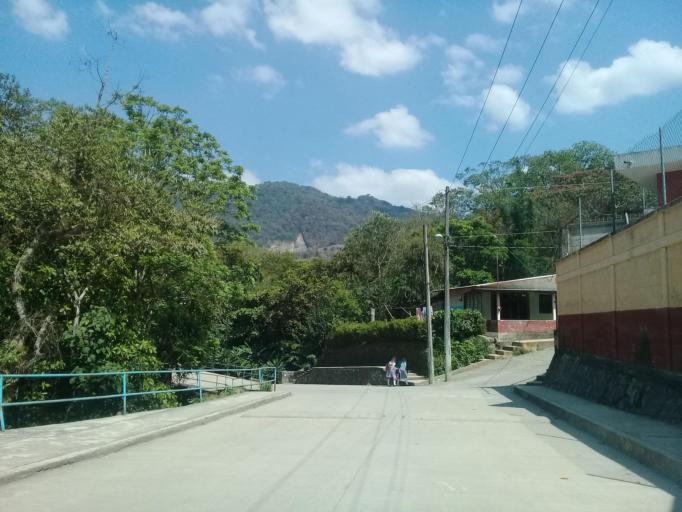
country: MX
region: Veracruz
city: Jalapilla
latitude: 18.8053
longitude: -97.0754
